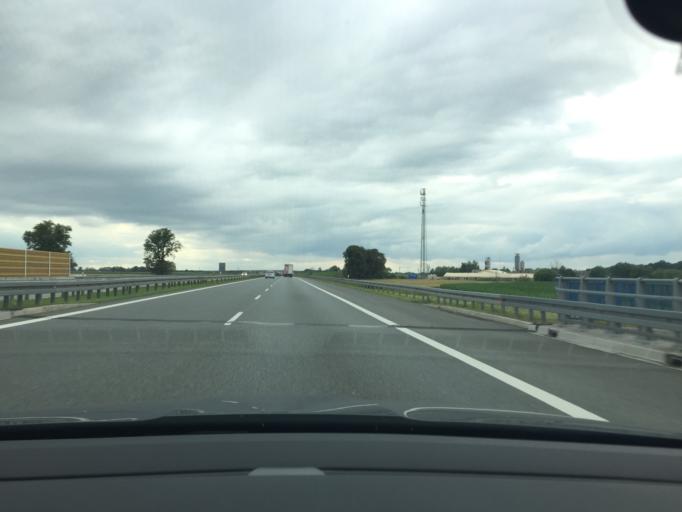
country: PL
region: Greater Poland Voivodeship
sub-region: Powiat szamotulski
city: Duszniki
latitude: 52.3901
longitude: 16.4429
